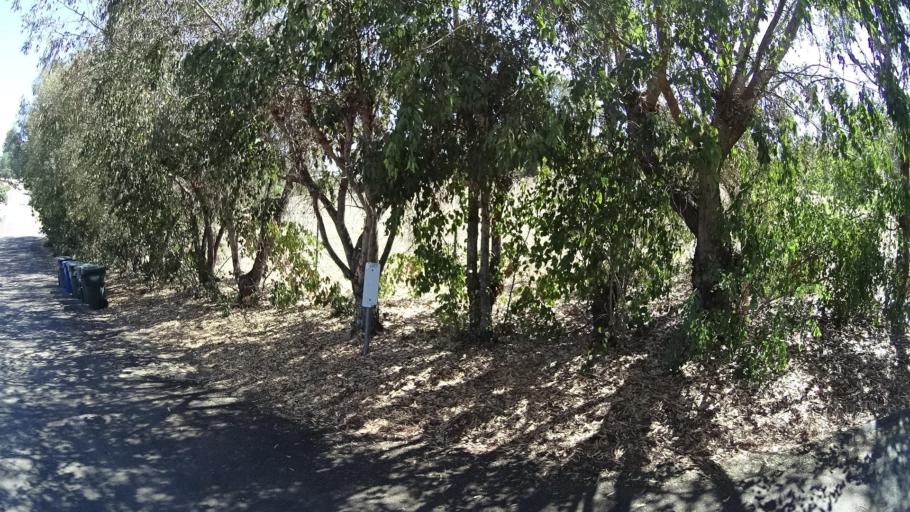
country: US
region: California
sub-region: San Diego County
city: Fallbrook
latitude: 33.3612
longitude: -117.2232
